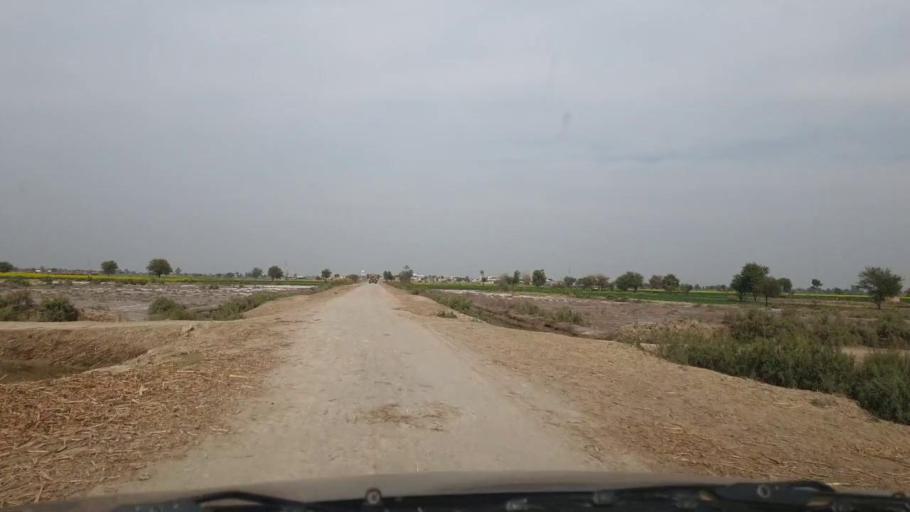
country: PK
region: Sindh
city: Sinjhoro
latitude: 26.0965
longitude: 68.8276
